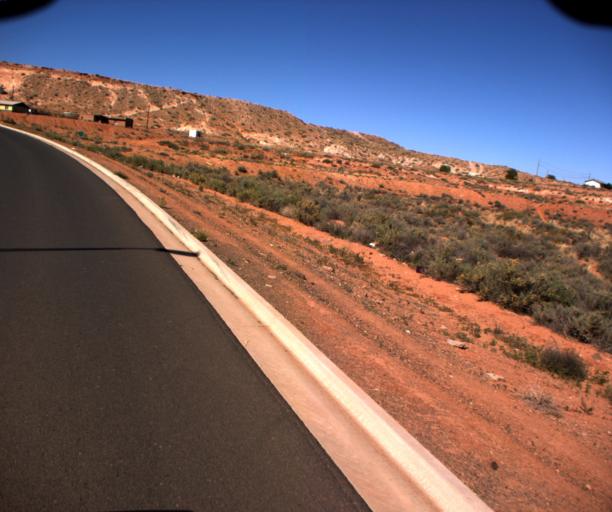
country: US
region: Arizona
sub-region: Coconino County
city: Tuba City
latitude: 36.1128
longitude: -111.2203
